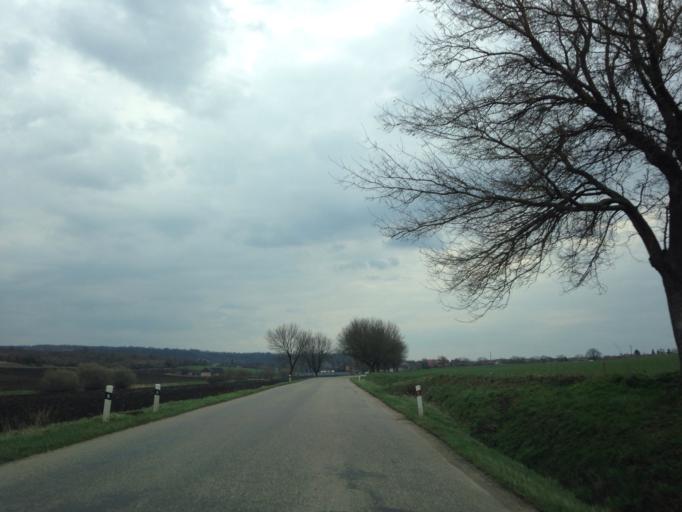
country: SK
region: Nitriansky
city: Svodin
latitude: 47.9709
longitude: 18.4077
